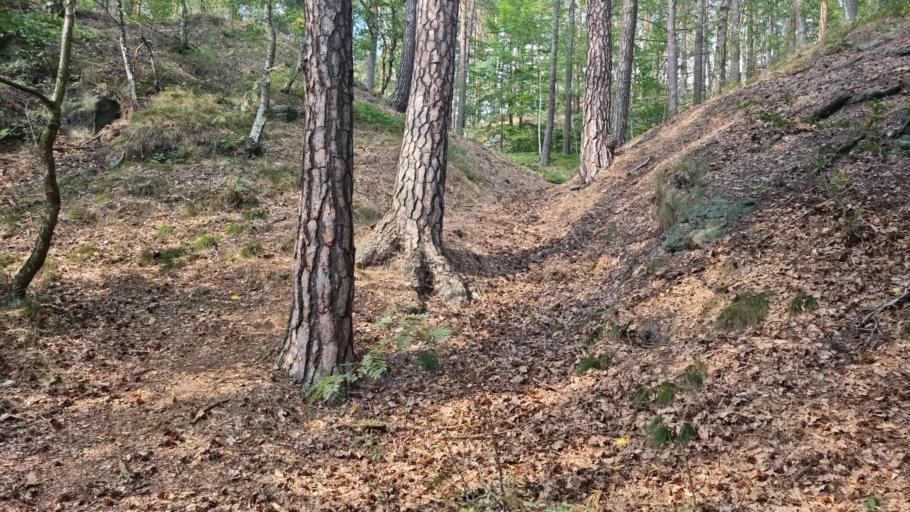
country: CZ
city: Cvikov
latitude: 50.7785
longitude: 14.6445
